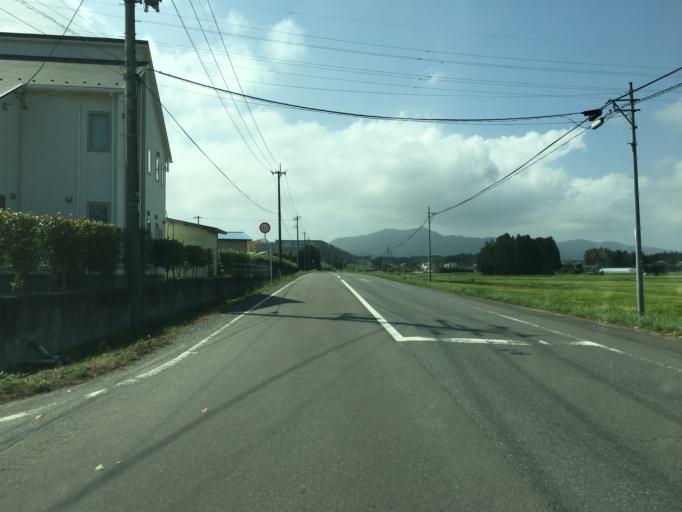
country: JP
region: Miyagi
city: Marumori
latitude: 37.8338
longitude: 140.9105
